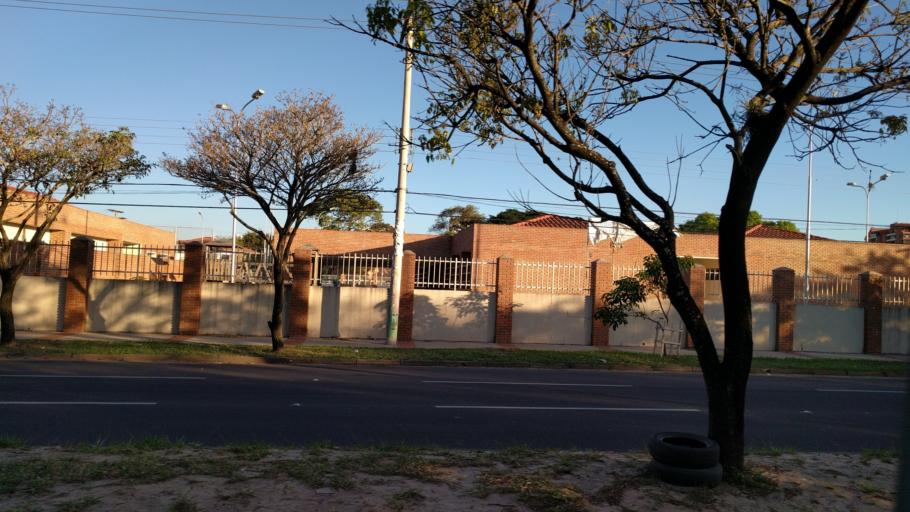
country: BO
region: Santa Cruz
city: Santa Cruz de la Sierra
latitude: -17.7614
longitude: -63.1893
